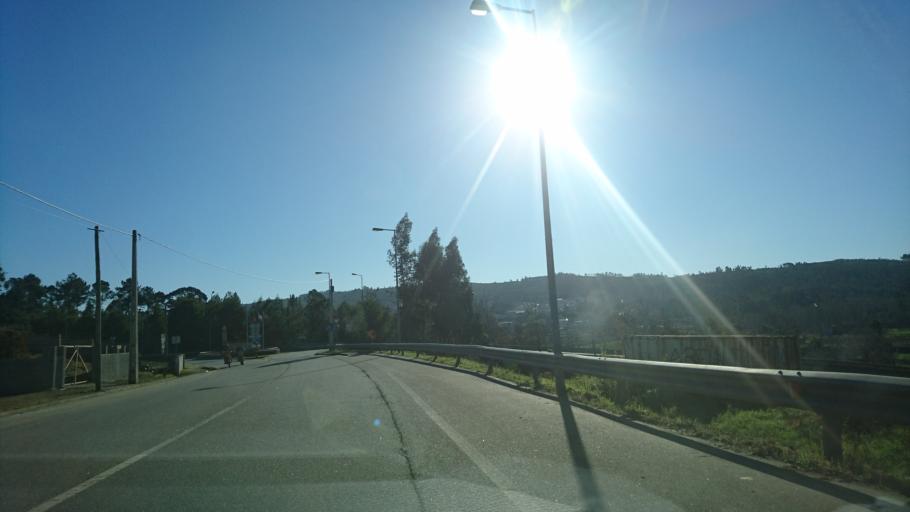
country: PT
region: Porto
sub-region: Paredes
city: Recarei
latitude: 41.1497
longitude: -8.3946
